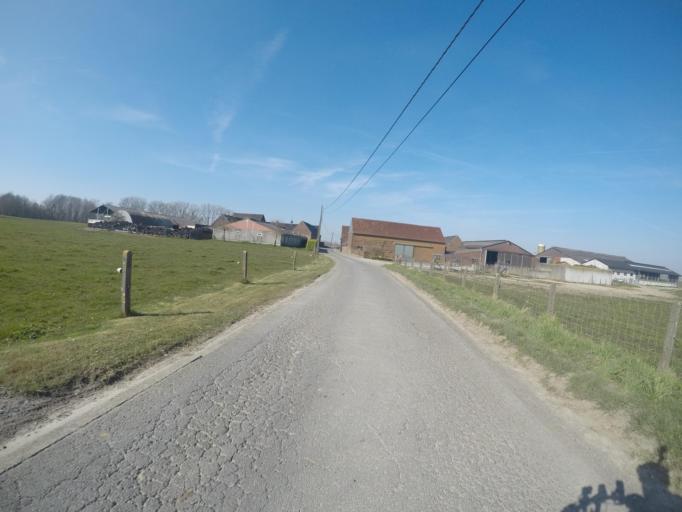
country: BE
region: Flanders
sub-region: Provincie Oost-Vlaanderen
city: Sint-Maria-Lierde
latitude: 50.7833
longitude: 3.8156
